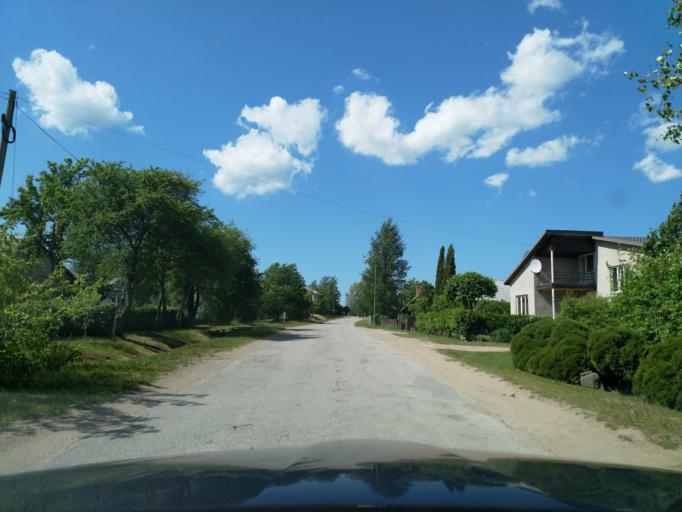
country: LV
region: Alsunga
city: Alsunga
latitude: 56.9731
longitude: 21.5678
